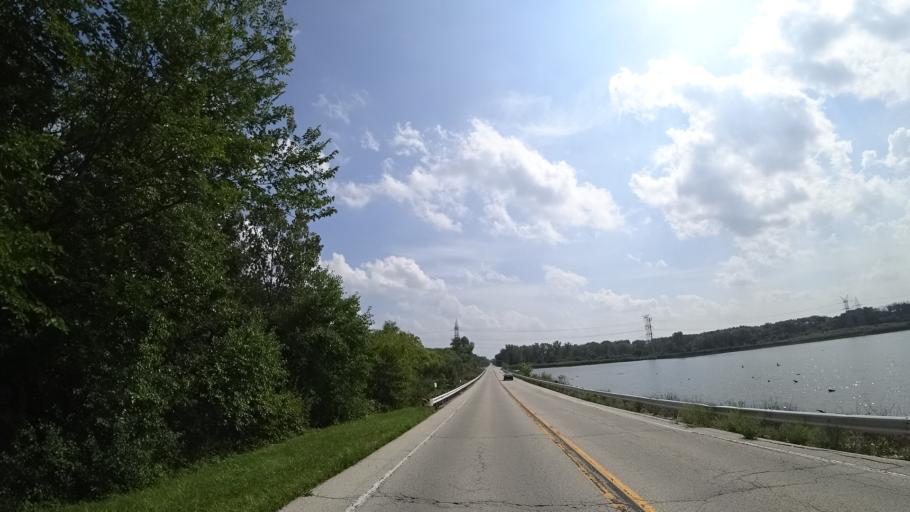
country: US
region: Illinois
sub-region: Will County
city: Goodings Grove
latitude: 41.6543
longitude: -87.9122
